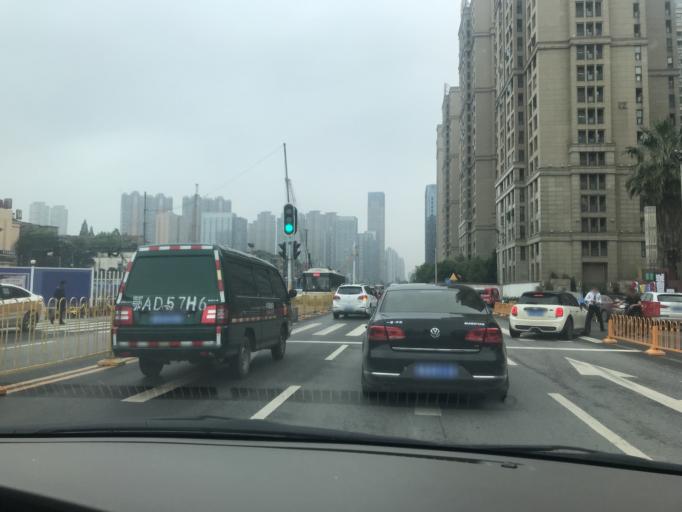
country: CN
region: Hubei
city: Jiang'an
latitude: 30.5846
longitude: 114.3203
